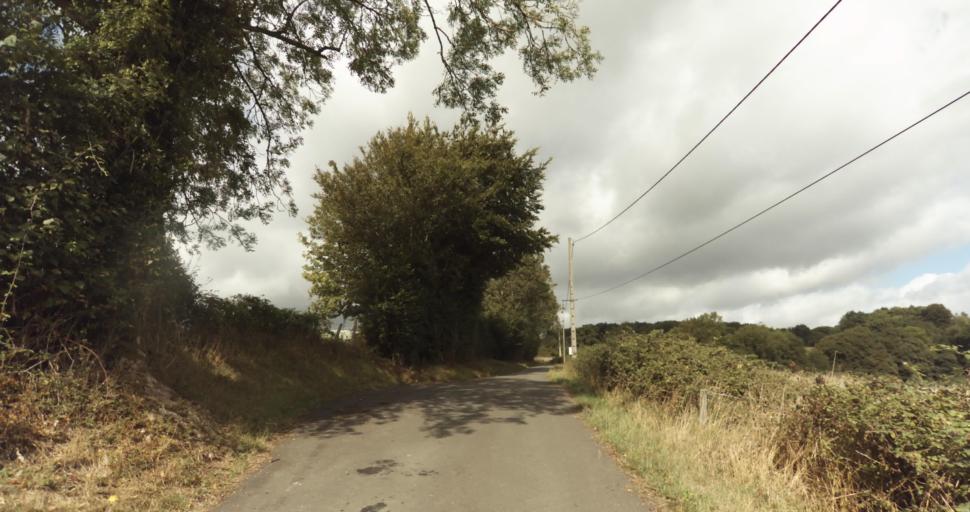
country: FR
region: Lower Normandy
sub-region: Departement de l'Orne
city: Gace
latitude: 48.8089
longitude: 0.2722
